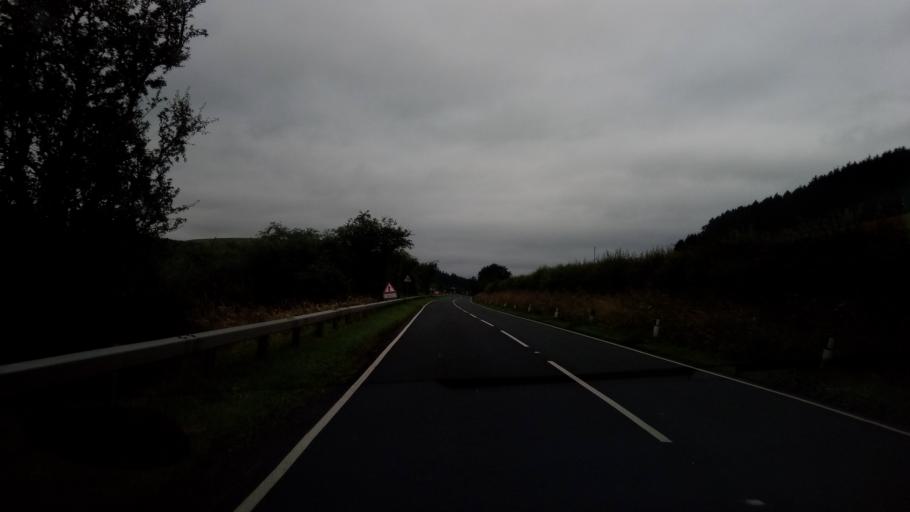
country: GB
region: Scotland
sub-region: The Scottish Borders
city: Hawick
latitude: 55.3652
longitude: -2.8880
